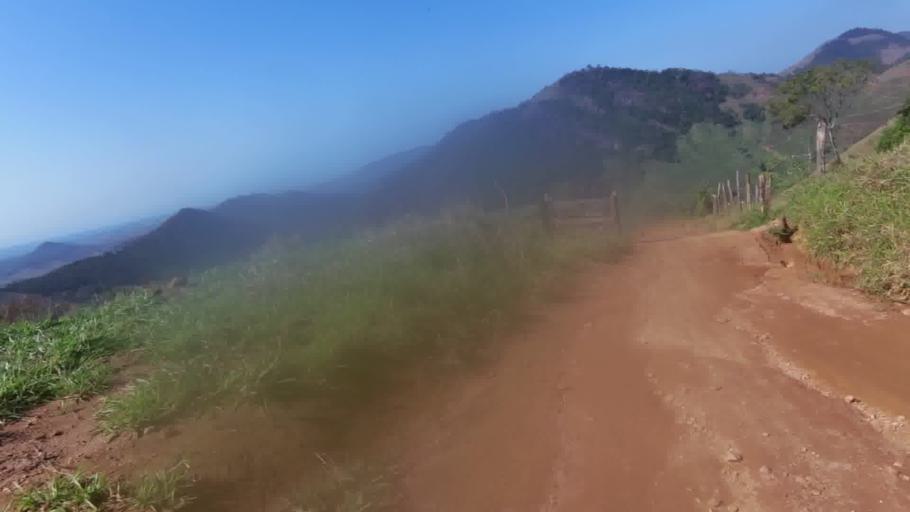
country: BR
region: Espirito Santo
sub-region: Alfredo Chaves
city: Alfredo Chaves
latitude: -20.6812
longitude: -40.7816
